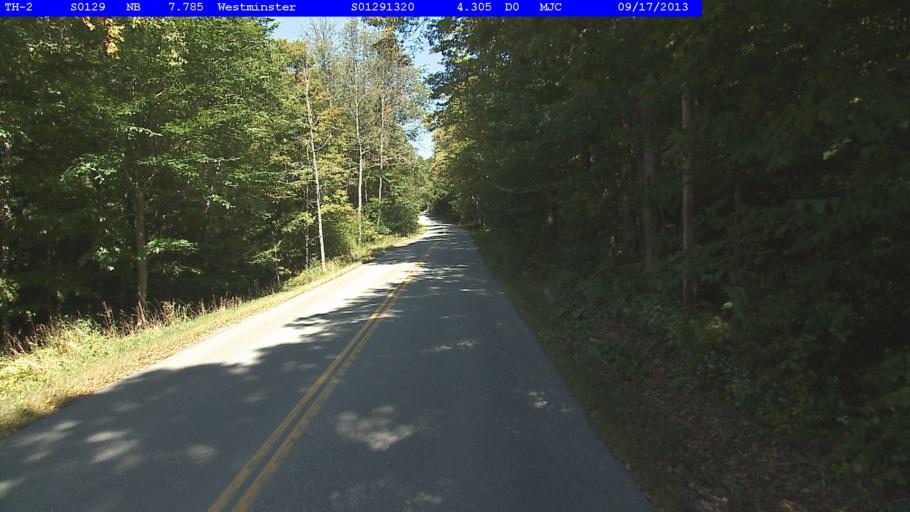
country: US
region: Vermont
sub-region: Windham County
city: Bellows Falls
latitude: 43.0772
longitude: -72.5377
